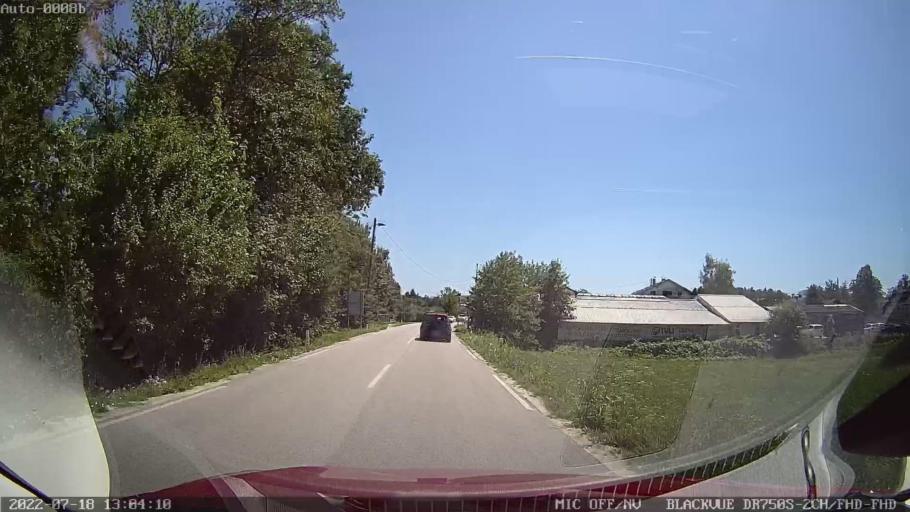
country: SI
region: Brezovica
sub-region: Opstina Ljubljana-Vic-Rudnik
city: Brezovica pri Ljubljani
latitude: 46.0466
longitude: 14.4405
